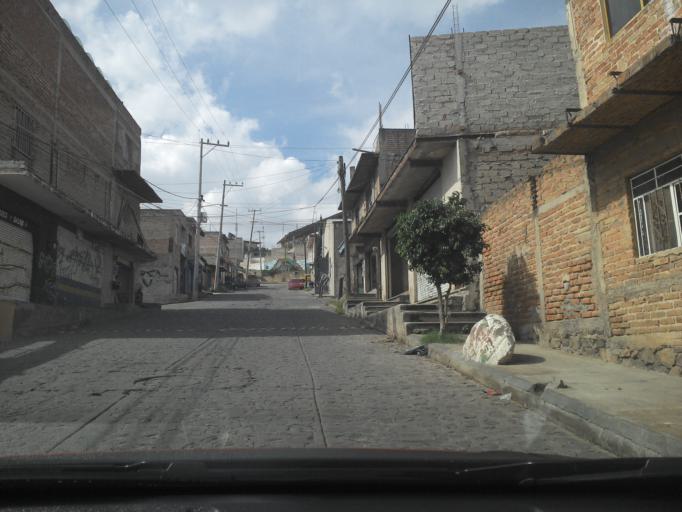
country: MX
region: Jalisco
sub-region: Tlajomulco de Zuniga
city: Altus Bosques
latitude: 20.5951
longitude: -103.3508
